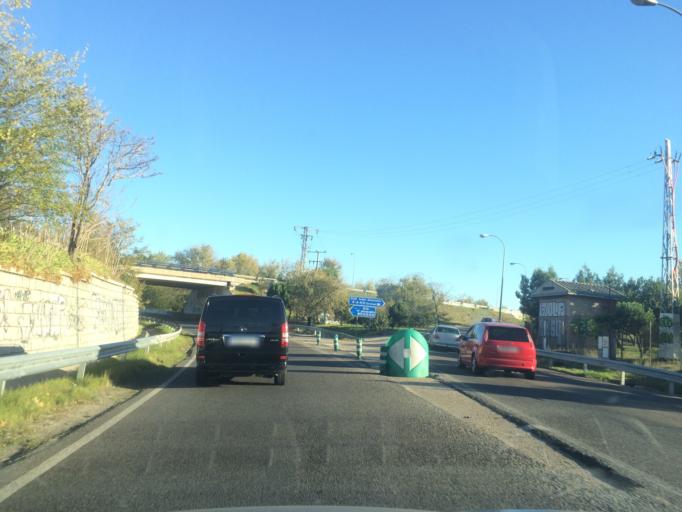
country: ES
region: Madrid
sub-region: Provincia de Madrid
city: San Blas
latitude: 40.4493
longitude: -3.5911
